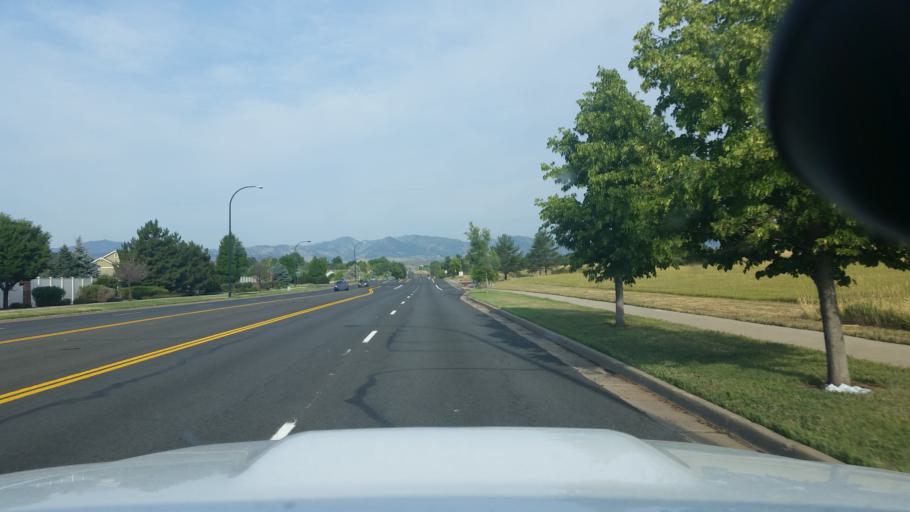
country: US
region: Colorado
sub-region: Broomfield County
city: Broomfield
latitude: 39.8928
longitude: -105.1012
